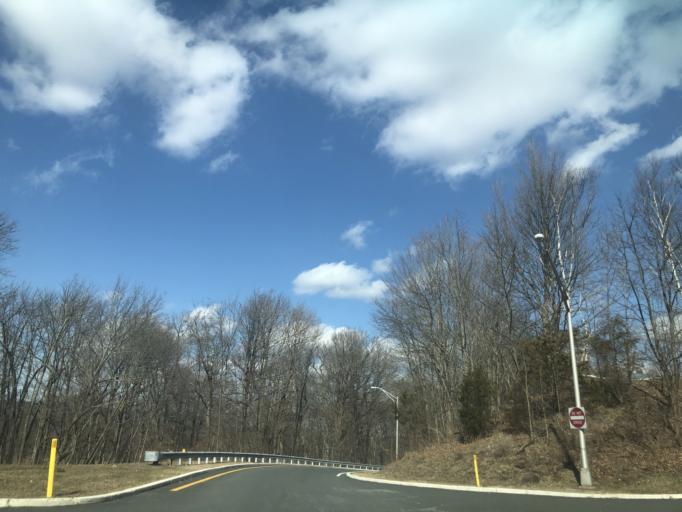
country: US
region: New Jersey
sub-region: Warren County
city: Belvidere
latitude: 40.9268
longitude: -75.0384
